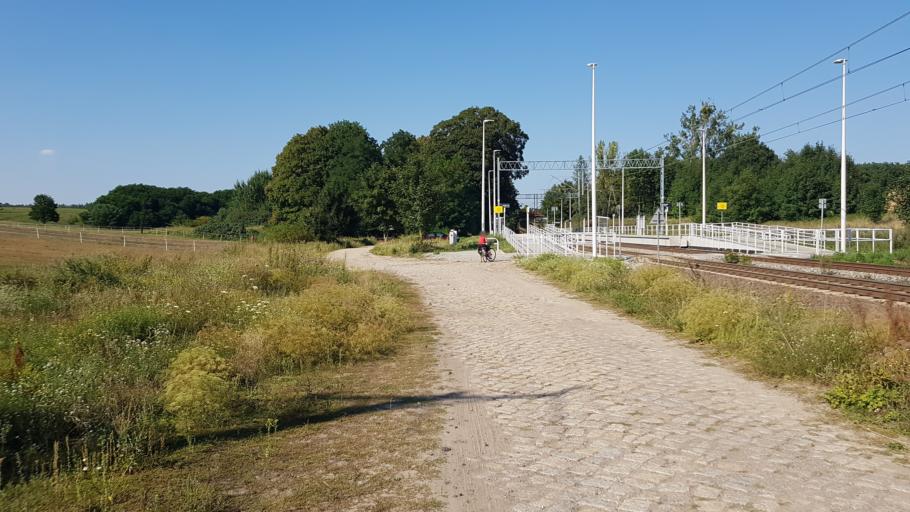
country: PL
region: West Pomeranian Voivodeship
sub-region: Powiat gryfinski
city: Gryfino
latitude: 53.1703
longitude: 14.4708
